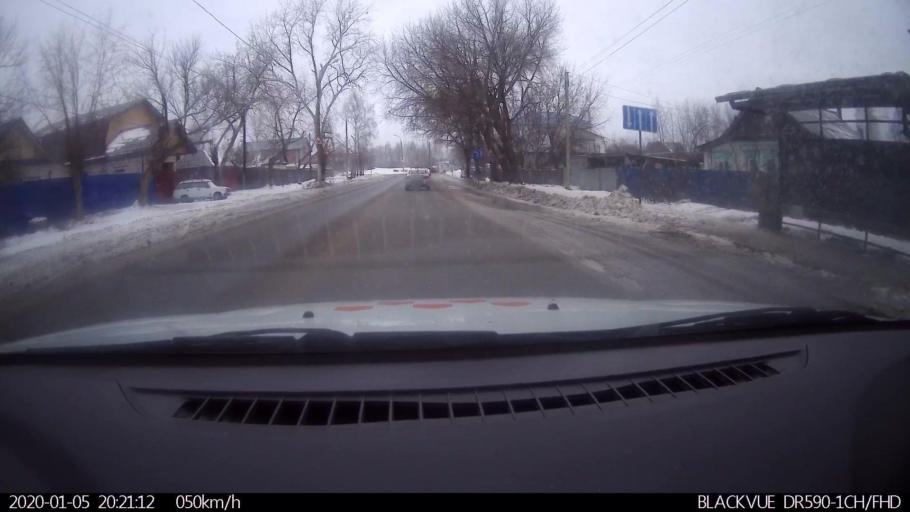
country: RU
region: Nizjnij Novgorod
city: Gorbatovka
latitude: 56.3733
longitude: 43.8079
